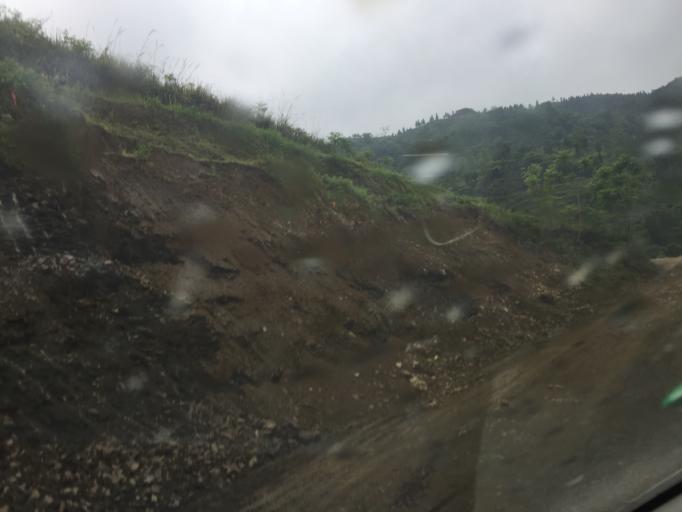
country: CN
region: Guizhou Sheng
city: Kuanping
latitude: 28.0046
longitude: 108.0426
